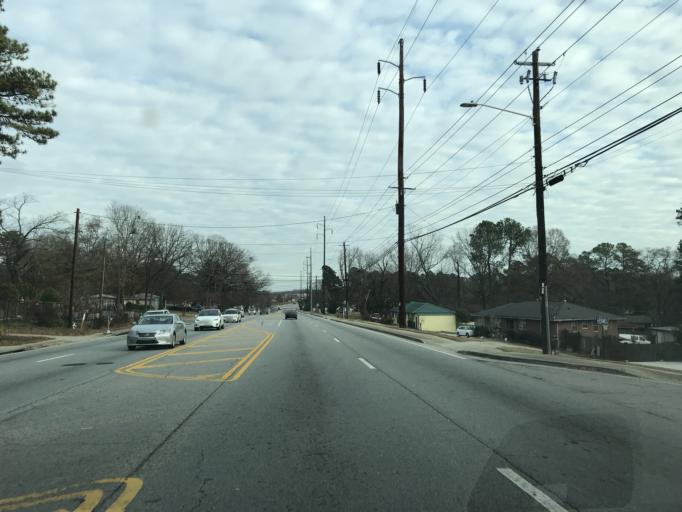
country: US
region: Georgia
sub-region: DeKalb County
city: Doraville
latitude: 33.8828
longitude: -84.2805
